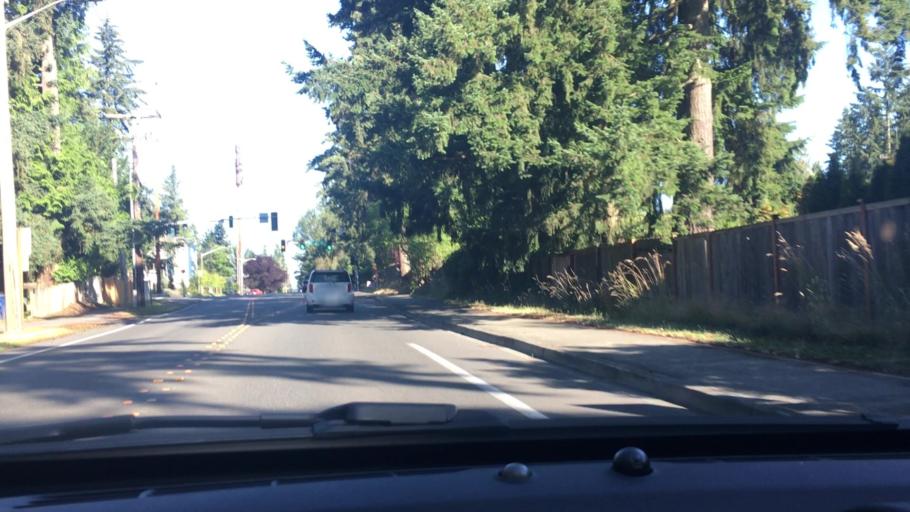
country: US
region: Washington
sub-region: King County
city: Sammamish
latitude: 47.6241
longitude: -122.1206
